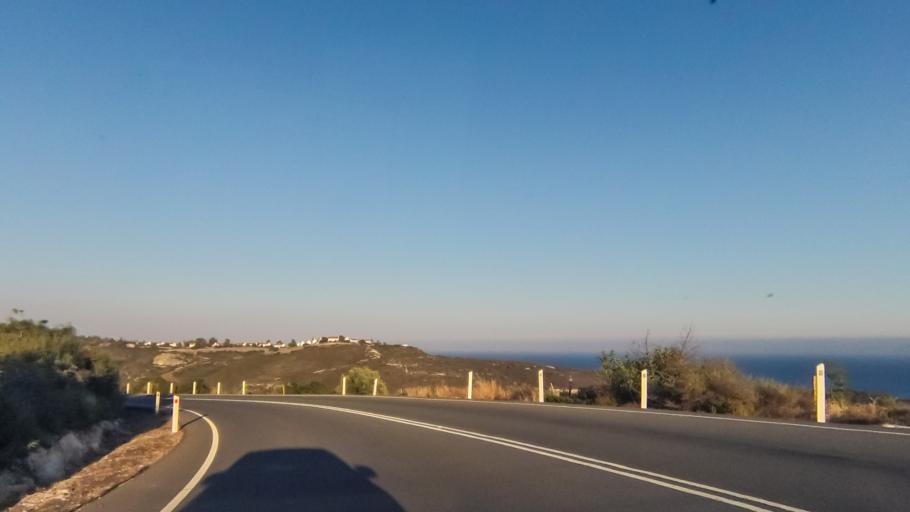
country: CY
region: Limassol
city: Sotira
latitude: 34.6719
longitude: 32.8127
